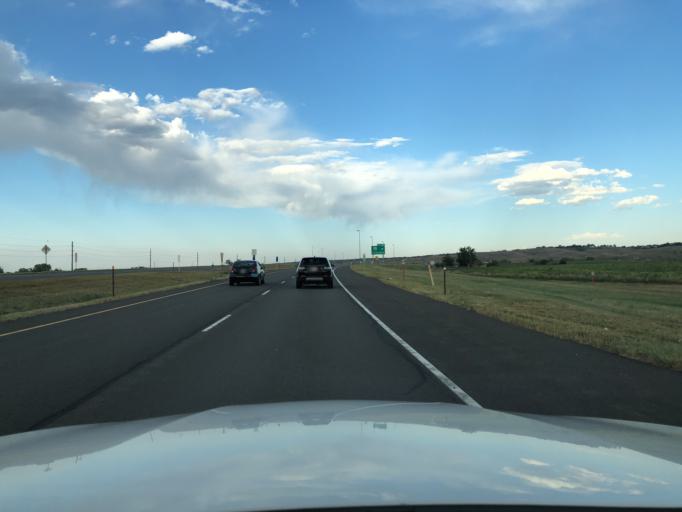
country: US
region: Colorado
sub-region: Boulder County
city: Louisville
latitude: 39.9572
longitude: -105.1067
